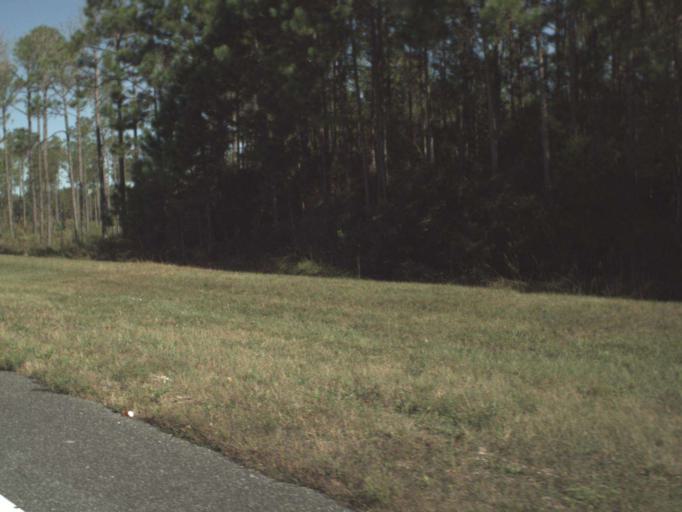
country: US
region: Florida
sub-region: Bay County
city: Laguna Beach
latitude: 30.2929
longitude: -86.0215
